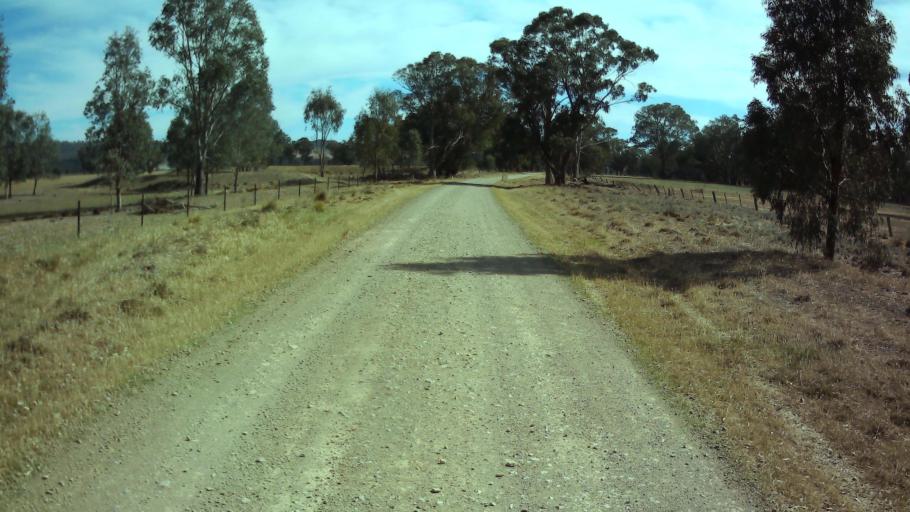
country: AU
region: New South Wales
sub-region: Weddin
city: Grenfell
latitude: -33.6918
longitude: 148.3038
